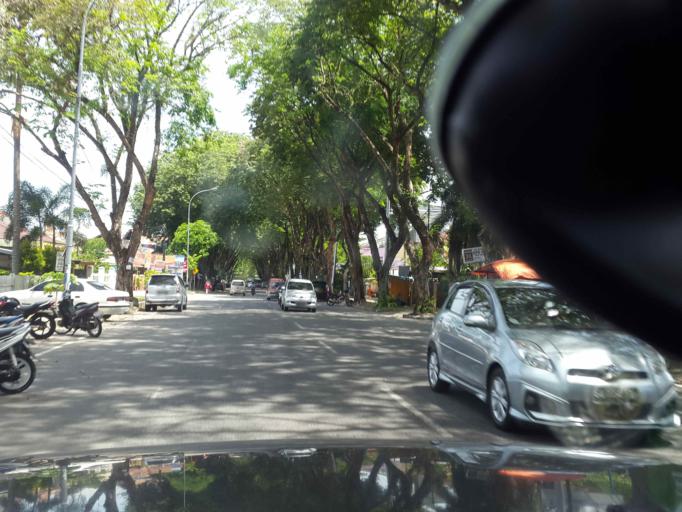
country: ID
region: West Sumatra
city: Padang
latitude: -0.9341
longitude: 100.3649
